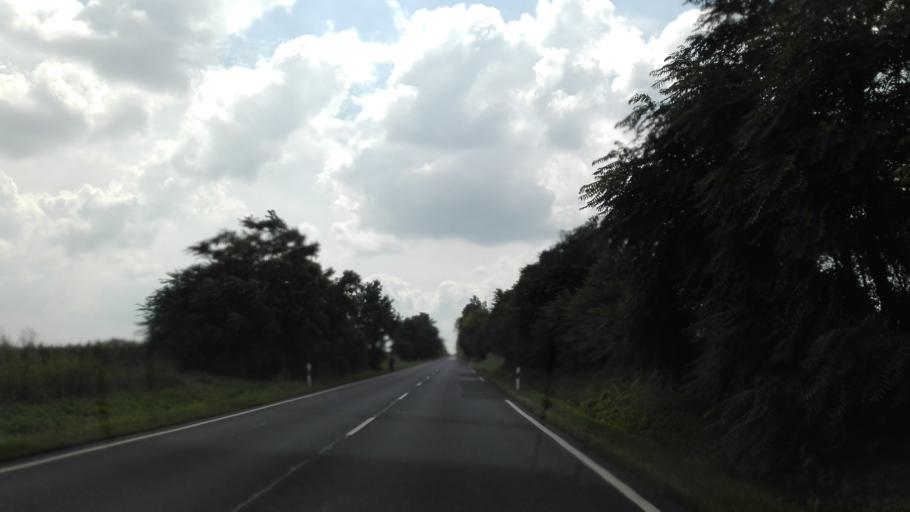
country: HU
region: Fejer
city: Eloszallas
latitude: 46.8235
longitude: 18.7980
